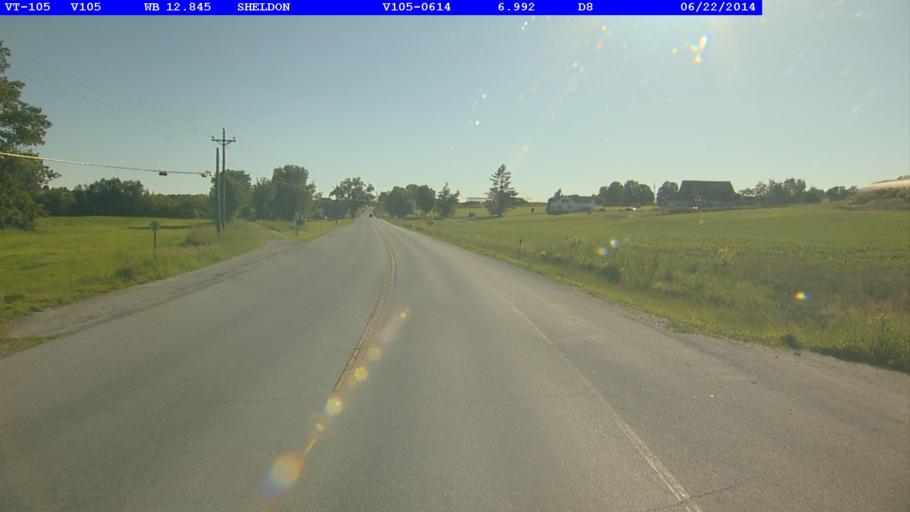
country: US
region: Vermont
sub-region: Franklin County
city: Enosburg Falls
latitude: 44.9119
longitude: -72.8995
